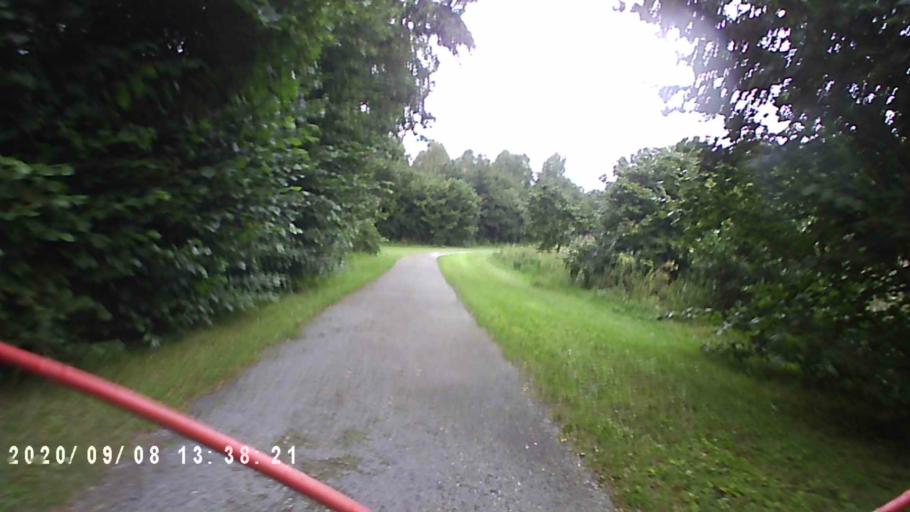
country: NL
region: Groningen
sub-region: Gemeente Veendam
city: Veendam
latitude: 53.1113
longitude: 6.8554
